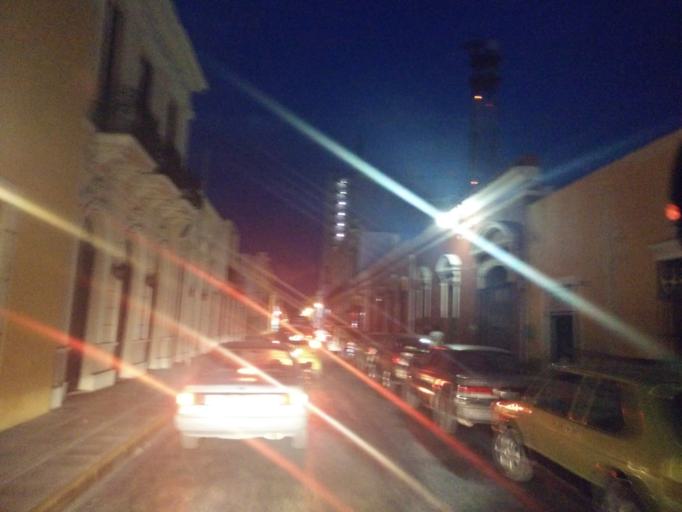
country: MX
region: Yucatan
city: Merida
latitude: 20.9693
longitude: -89.6266
